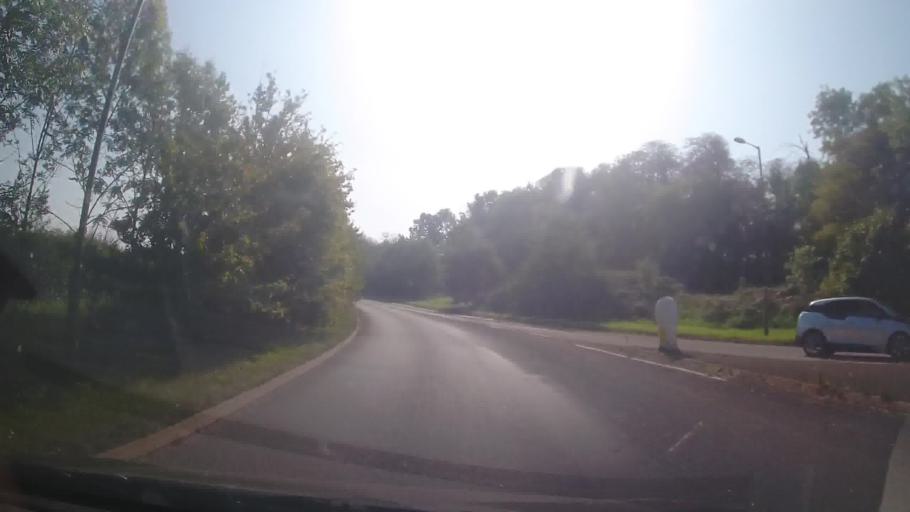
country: GB
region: England
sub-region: Worcestershire
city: Evesham
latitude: 52.1132
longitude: -1.9600
